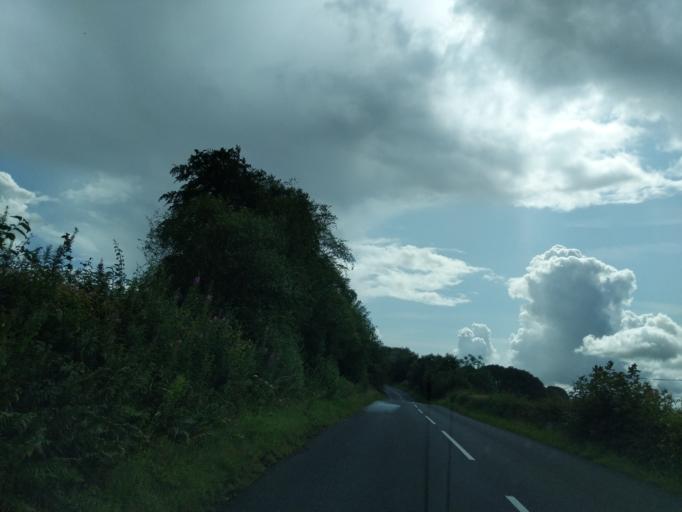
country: GB
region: Scotland
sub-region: East Renfrewshire
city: Neilston
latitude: 55.7489
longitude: -4.4626
